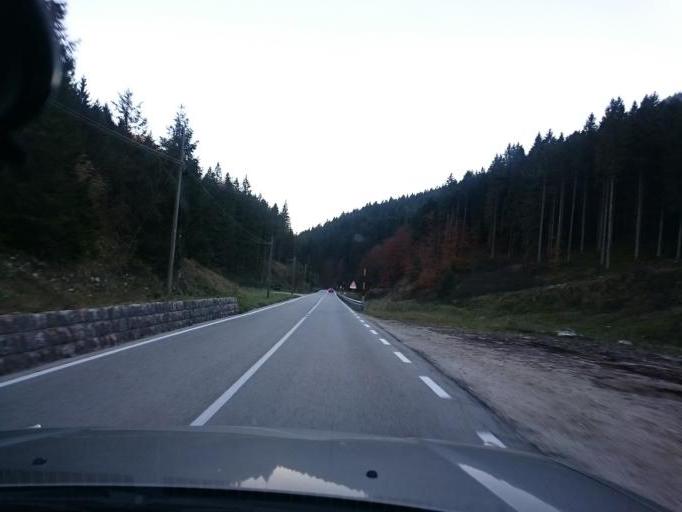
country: IT
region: Veneto
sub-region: Provincia di Vicenza
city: Roana
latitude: 45.9328
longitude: 11.4435
